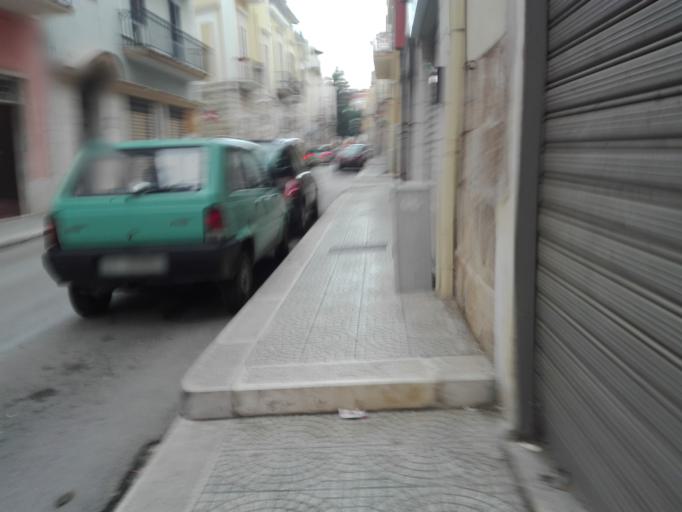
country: IT
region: Apulia
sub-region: Provincia di Bari
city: Corato
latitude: 41.1557
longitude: 16.4097
